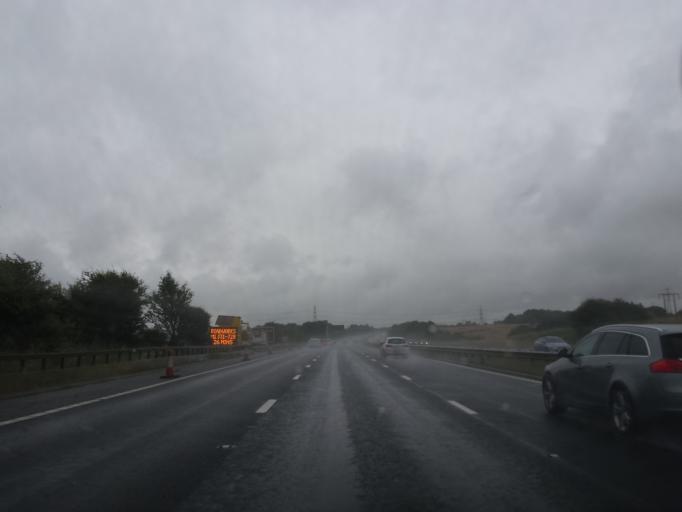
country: GB
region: England
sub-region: Rotherham
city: Bramley
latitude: 53.4142
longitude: -1.2558
